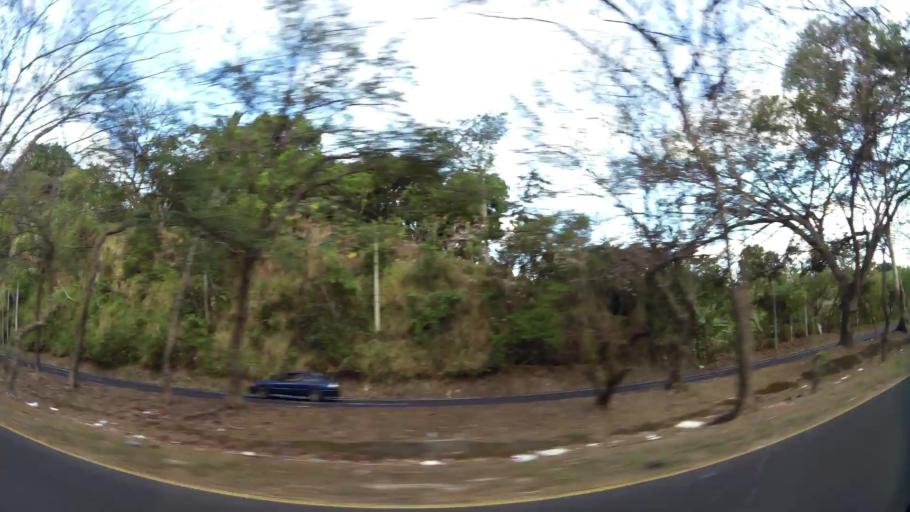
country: SV
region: San Vicente
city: San Sebastian
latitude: 13.7141
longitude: -88.8581
